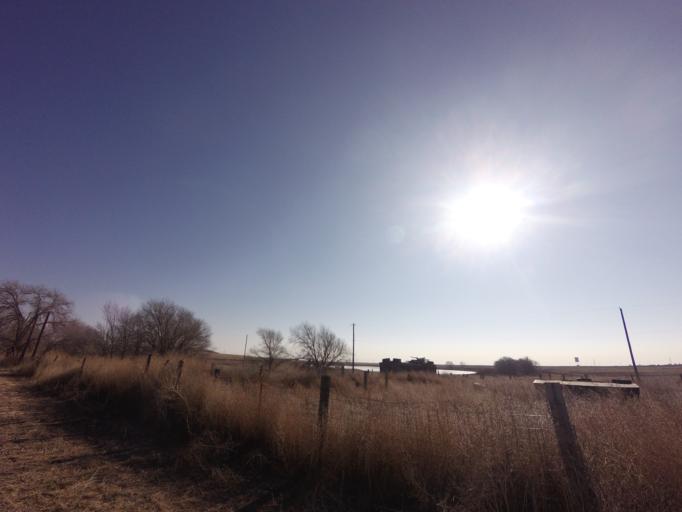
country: US
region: New Mexico
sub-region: Curry County
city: Clovis
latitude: 34.3845
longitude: -103.1823
